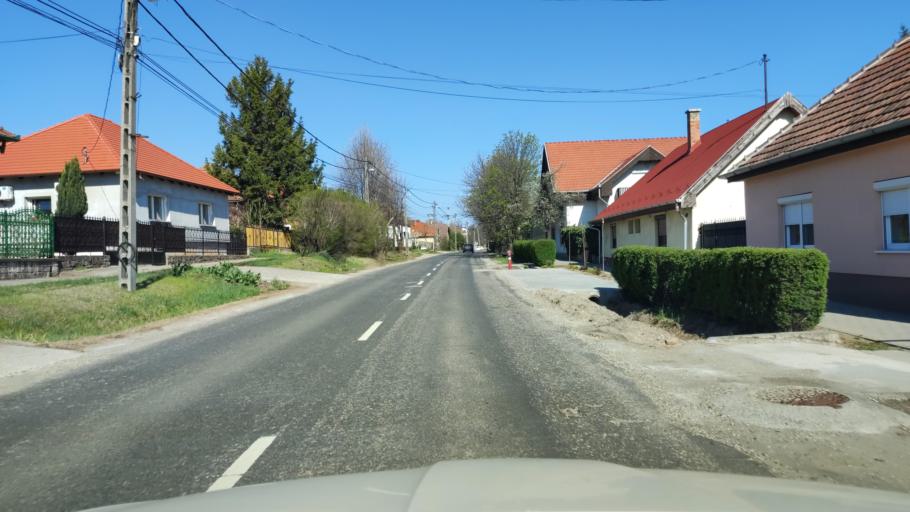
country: HU
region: Pest
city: Kistarcsa
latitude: 47.5433
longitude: 19.2656
